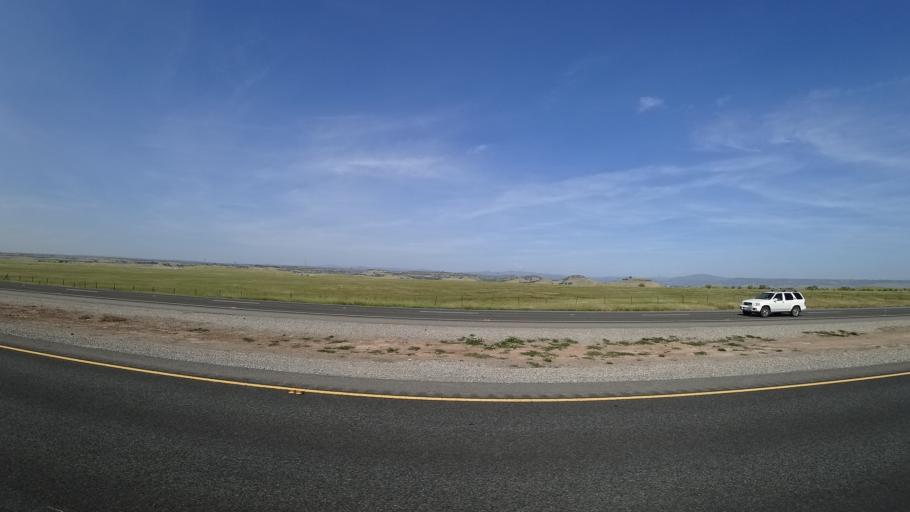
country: US
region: California
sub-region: Butte County
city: Durham
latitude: 39.6358
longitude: -121.7090
